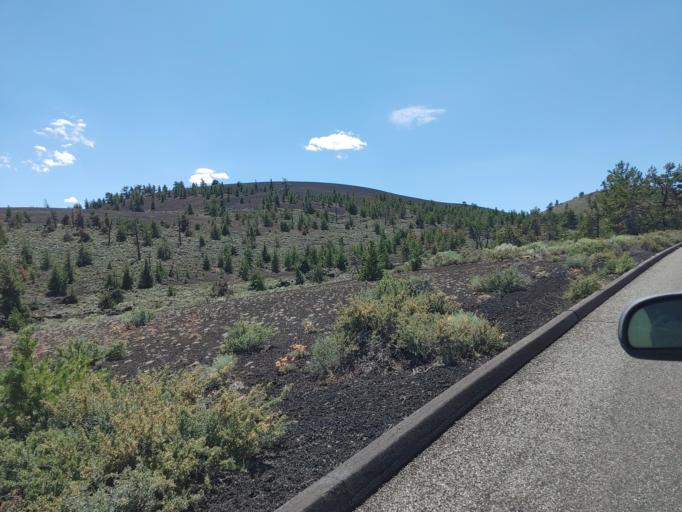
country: US
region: Idaho
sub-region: Butte County
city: Arco
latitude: 43.4473
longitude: -113.5483
